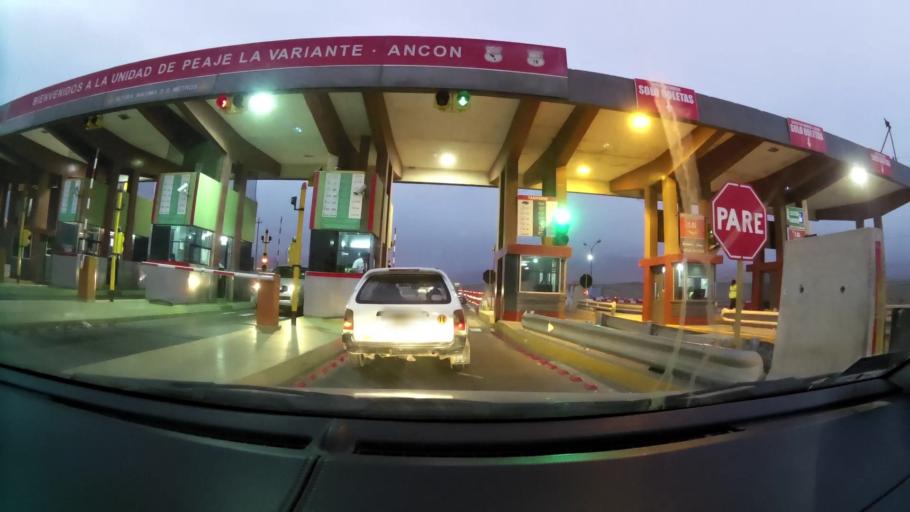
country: PE
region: Lima
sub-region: Lima
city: Santa Rosa
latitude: -11.7477
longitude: -77.1438
